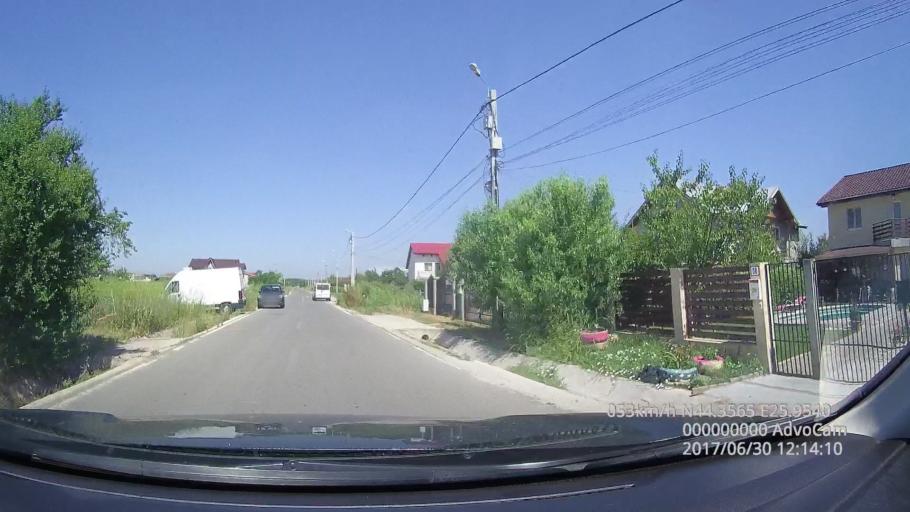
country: RO
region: Ilfov
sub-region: Comuna Clinceni
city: Clinceni
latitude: 44.3567
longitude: 25.9536
